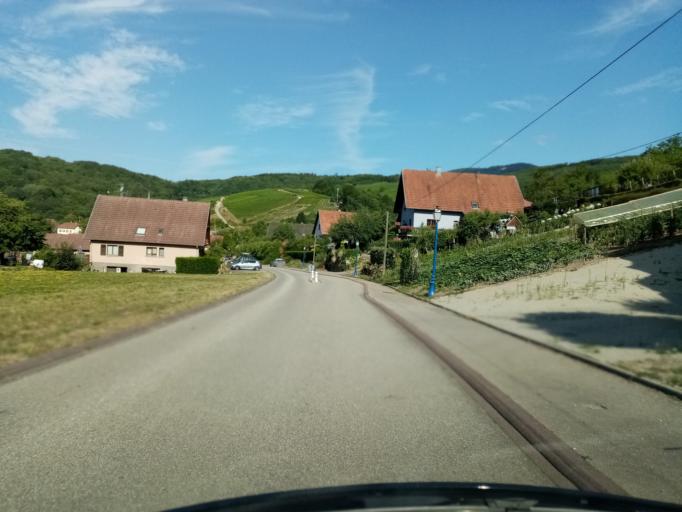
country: FR
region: Alsace
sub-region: Departement du Bas-Rhin
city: Ville
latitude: 48.3559
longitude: 7.3222
